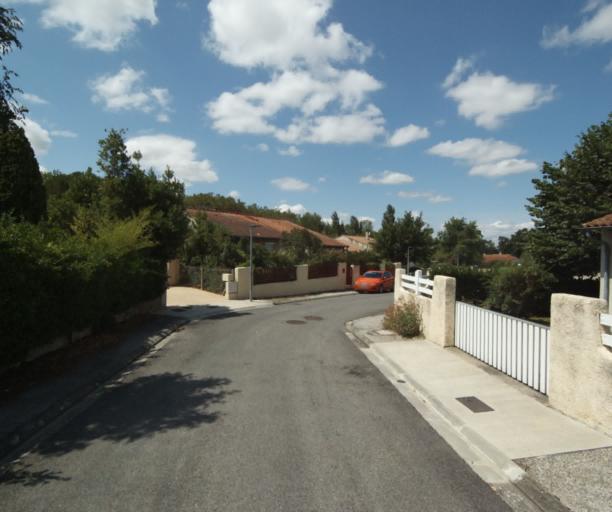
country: FR
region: Midi-Pyrenees
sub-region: Departement de la Haute-Garonne
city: Revel
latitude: 43.4501
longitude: 2.0070
